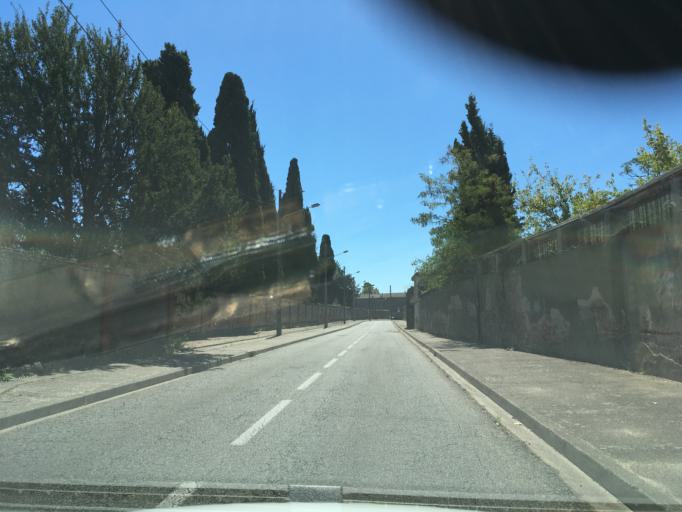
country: FR
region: Midi-Pyrenees
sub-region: Departement du Tarn-et-Garonne
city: Montauban
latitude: 44.0264
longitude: 1.3487
